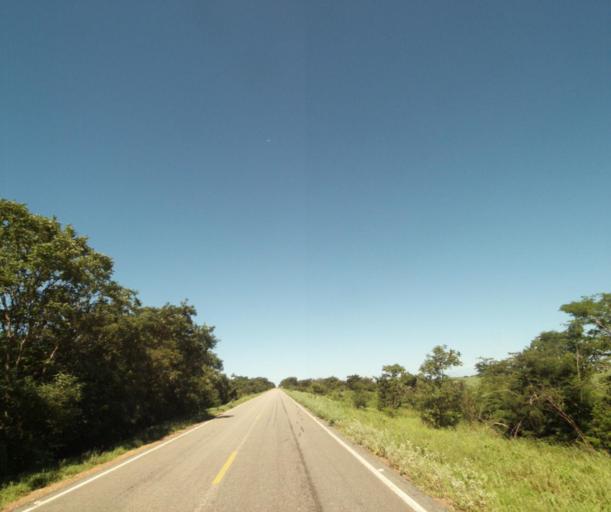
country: BR
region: Bahia
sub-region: Palmas De Monte Alto
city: Palmas de Monte Alto
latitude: -14.2638
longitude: -43.3372
